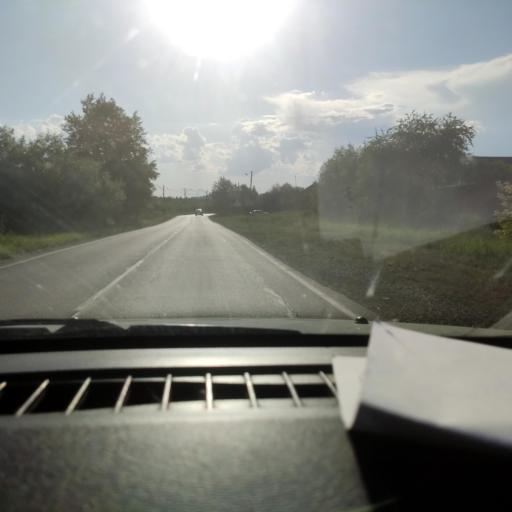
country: RU
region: Perm
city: Krasnokamsk
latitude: 58.1338
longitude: 55.7490
